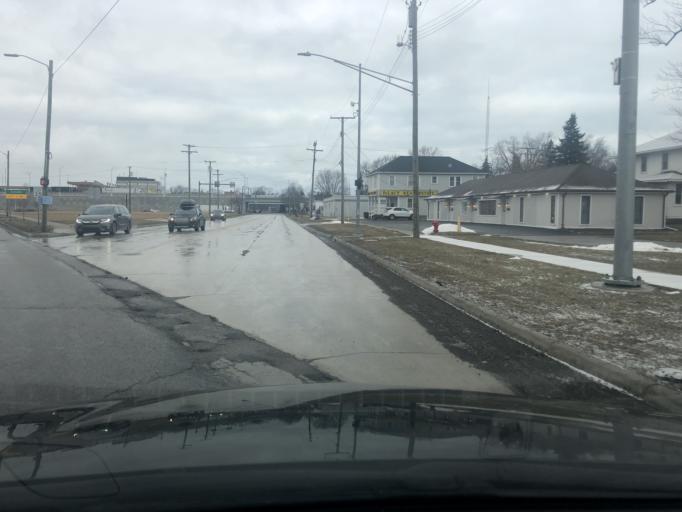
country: US
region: Michigan
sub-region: Saint Clair County
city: Port Huron
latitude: 42.9954
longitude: -82.4342
